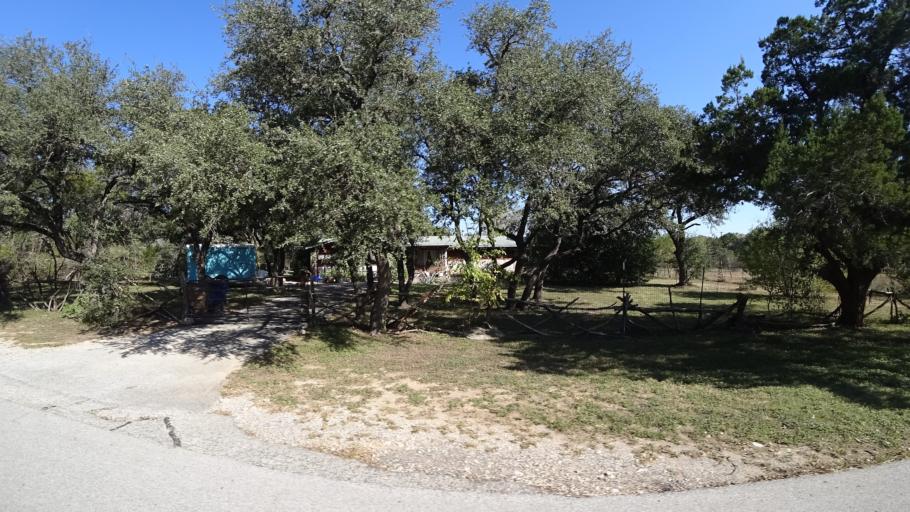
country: US
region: Texas
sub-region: Travis County
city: Barton Creek
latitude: 30.2276
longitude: -97.8551
